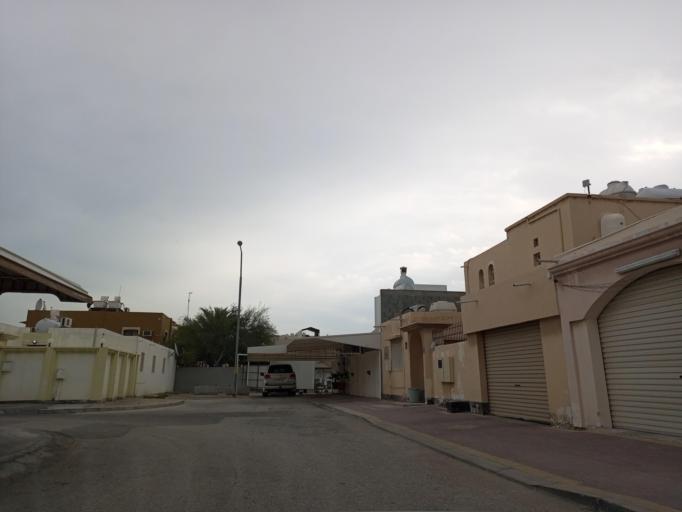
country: BH
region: Muharraq
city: Al Muharraq
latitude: 26.2592
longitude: 50.6325
